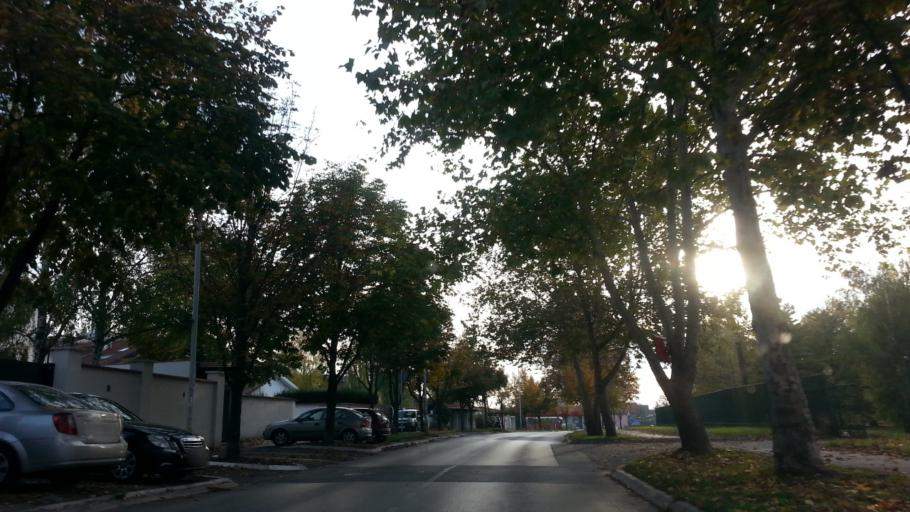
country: RS
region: Central Serbia
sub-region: Belgrade
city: Zemun
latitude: 44.8148
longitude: 20.3824
